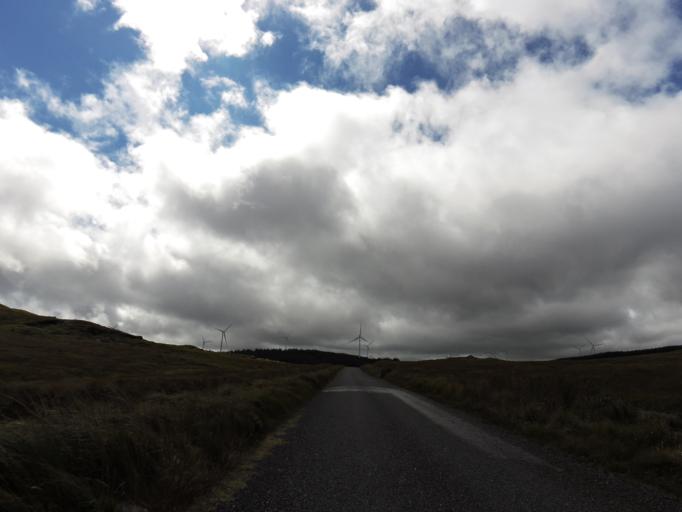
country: IE
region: Connaught
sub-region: County Galway
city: Oughterard
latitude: 53.3867
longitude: -9.3567
